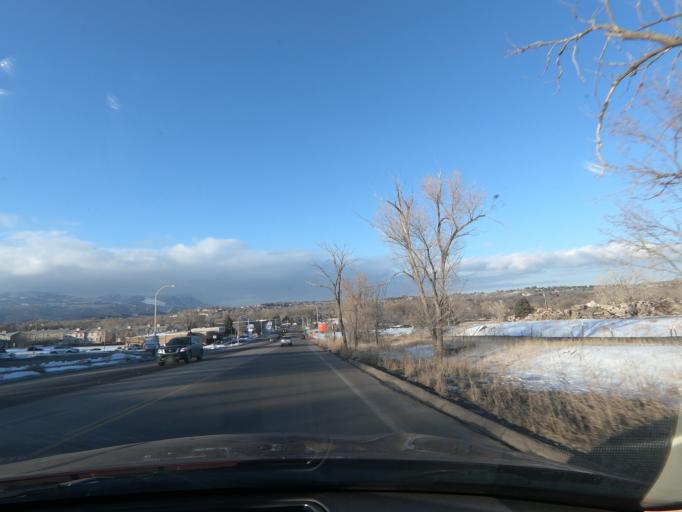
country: US
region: Colorado
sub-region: El Paso County
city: Colorado Springs
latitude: 38.8364
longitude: -104.8591
